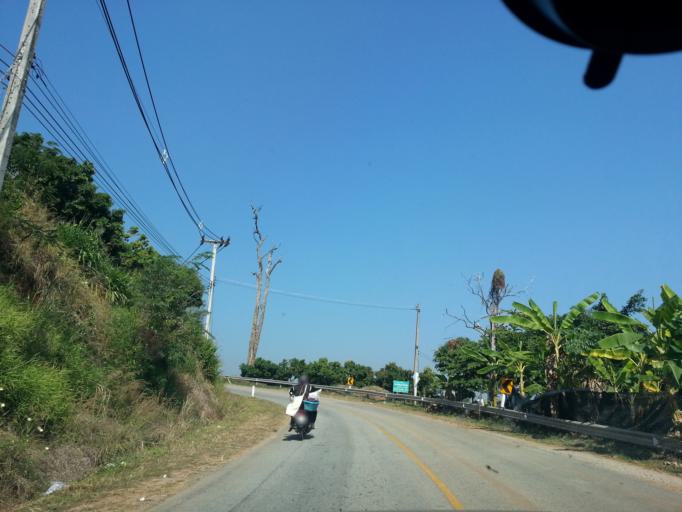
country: TH
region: Chiang Mai
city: Chai Prakan
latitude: 19.8282
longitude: 99.1031
